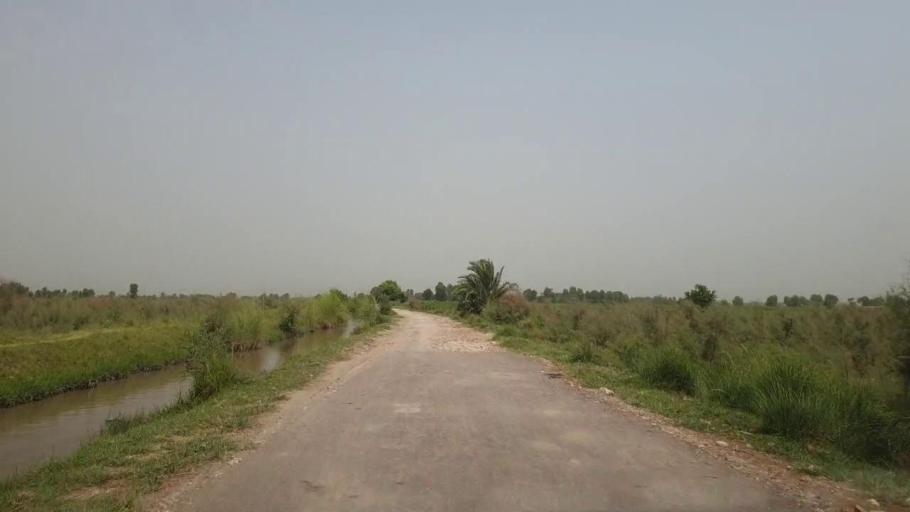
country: PK
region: Sindh
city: Gambat
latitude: 27.4503
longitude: 68.4429
